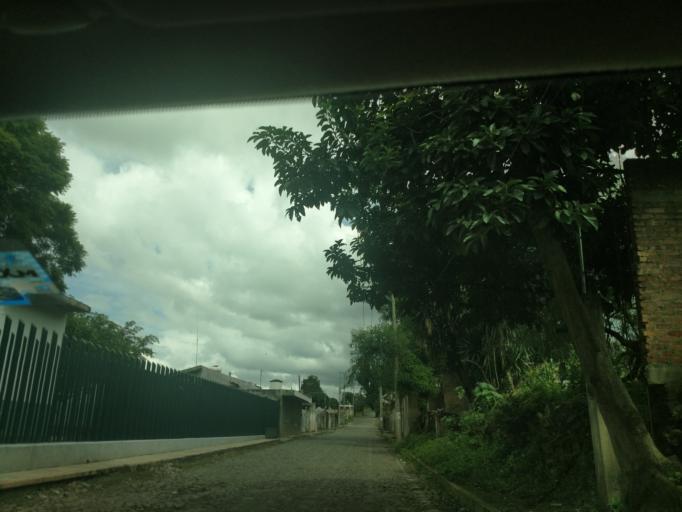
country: MX
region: Nayarit
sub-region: Tepic
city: La Corregidora
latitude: 21.4494
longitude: -104.8118
